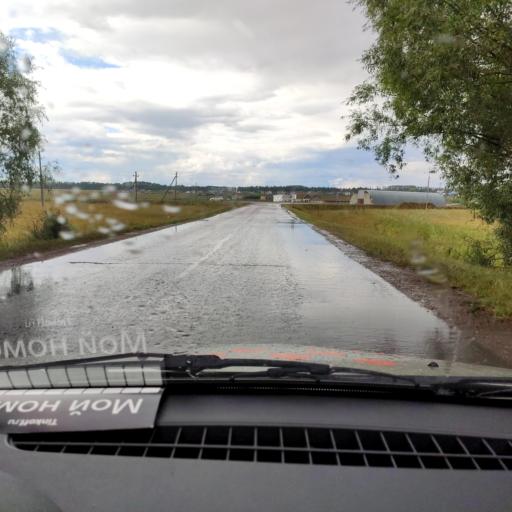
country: RU
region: Bashkortostan
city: Avdon
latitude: 54.5085
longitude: 55.8770
